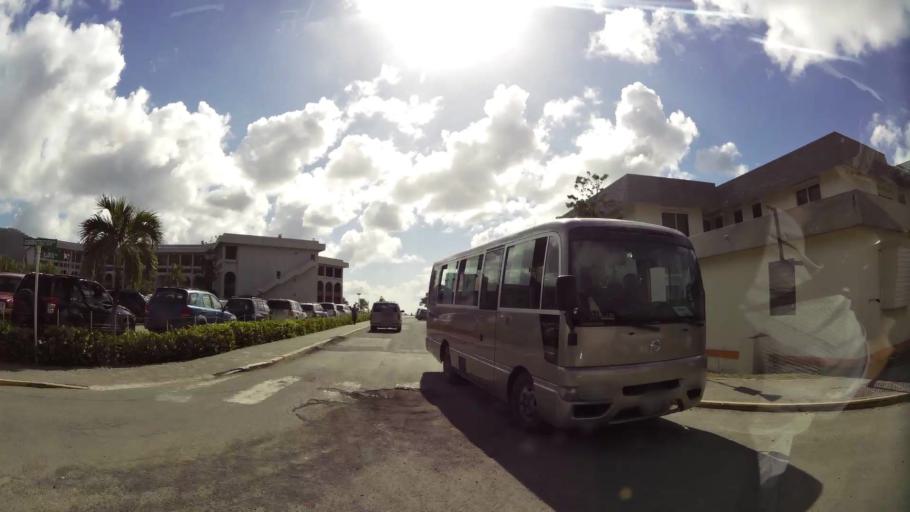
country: VG
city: Road Town
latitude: 18.4215
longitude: -64.6173
